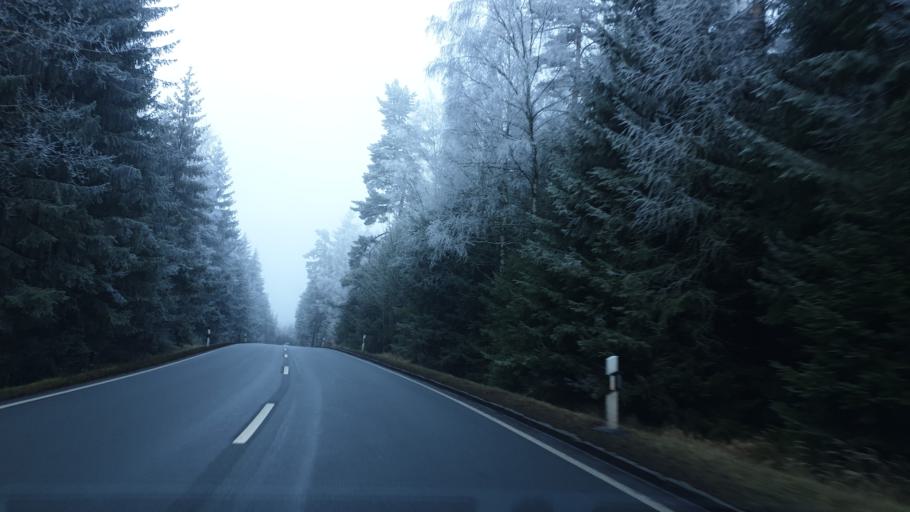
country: DE
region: Saxony
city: Bad Brambach
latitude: 50.1990
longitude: 12.3153
